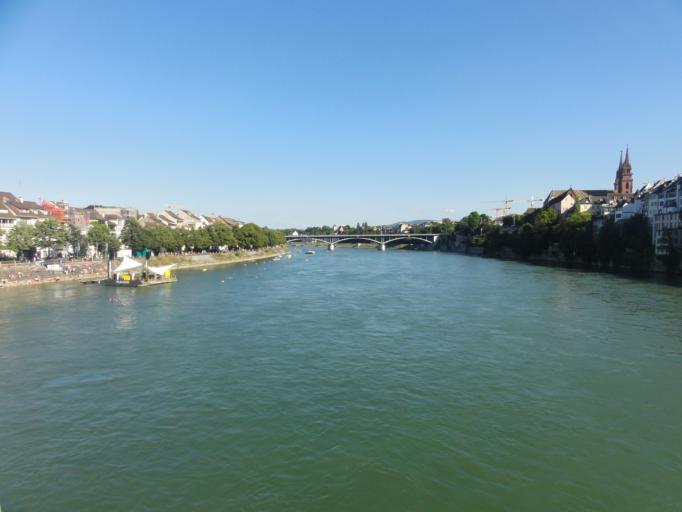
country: CH
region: Basel-City
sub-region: Basel-Stadt
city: Basel
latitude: 47.5598
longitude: 7.5892
